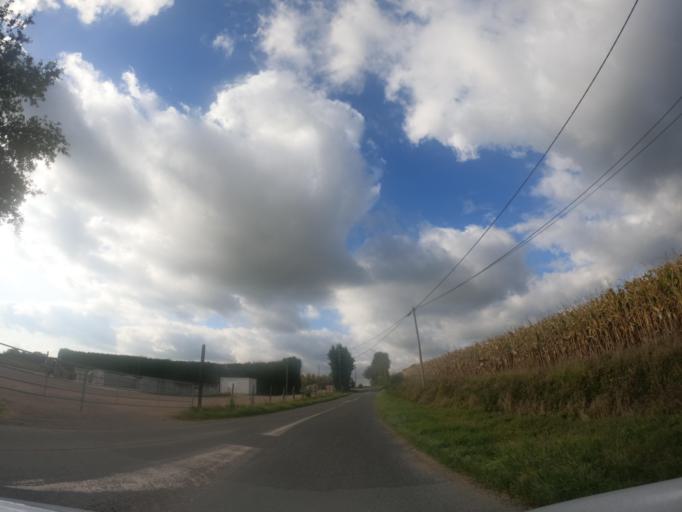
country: FR
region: Poitou-Charentes
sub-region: Departement des Deux-Sevres
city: La Foret-sur-Sevre
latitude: 46.7895
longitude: -0.6102
